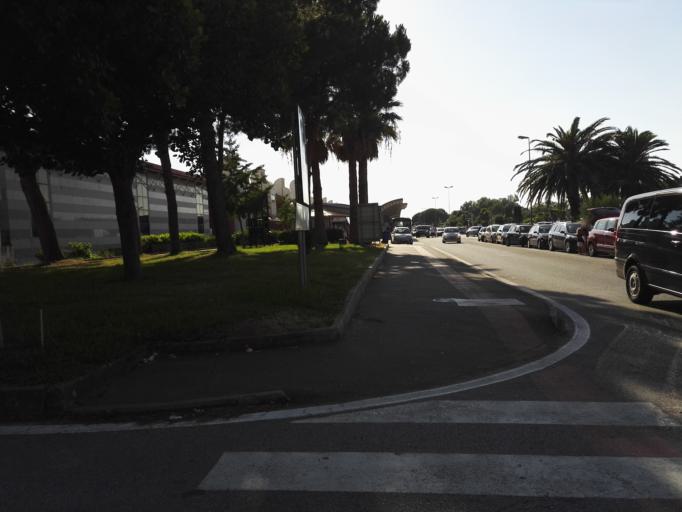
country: IT
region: Calabria
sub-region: Provincia di Catanzaro
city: Santa Eufemia Lamezia
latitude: 38.9097
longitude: 16.2472
